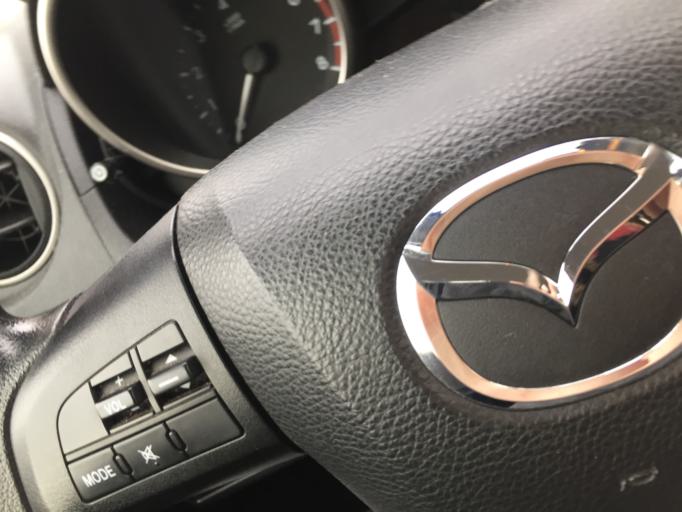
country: US
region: Massachusetts
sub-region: Hampden County
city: Westfield
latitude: 42.1338
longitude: -72.7405
